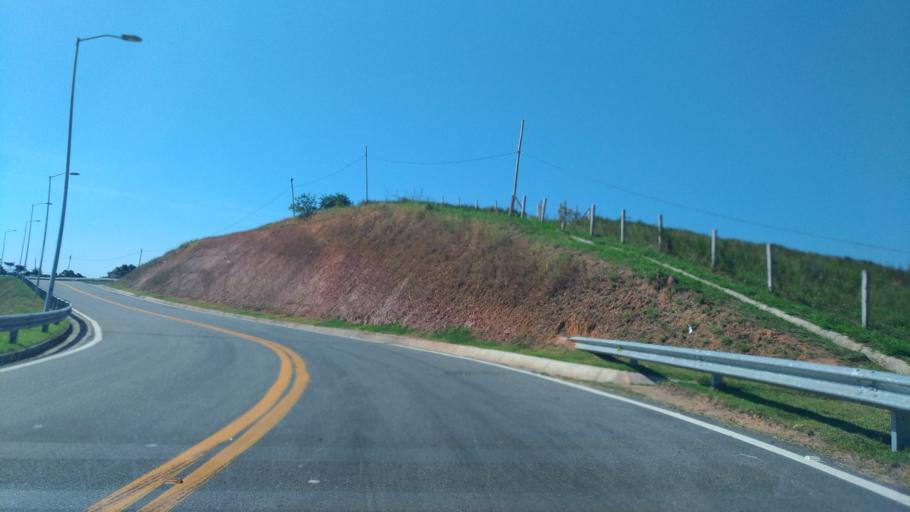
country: BR
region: Rio de Janeiro
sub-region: Sao Fidelis
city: Sao Fidelis
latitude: -21.9825
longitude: -41.6597
